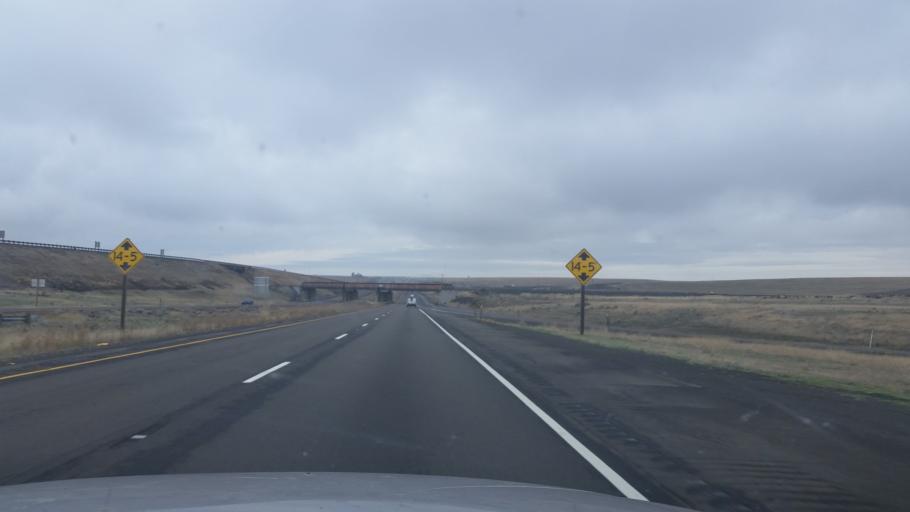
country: US
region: Washington
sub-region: Adams County
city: Ritzville
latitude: 47.1115
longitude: -118.3956
